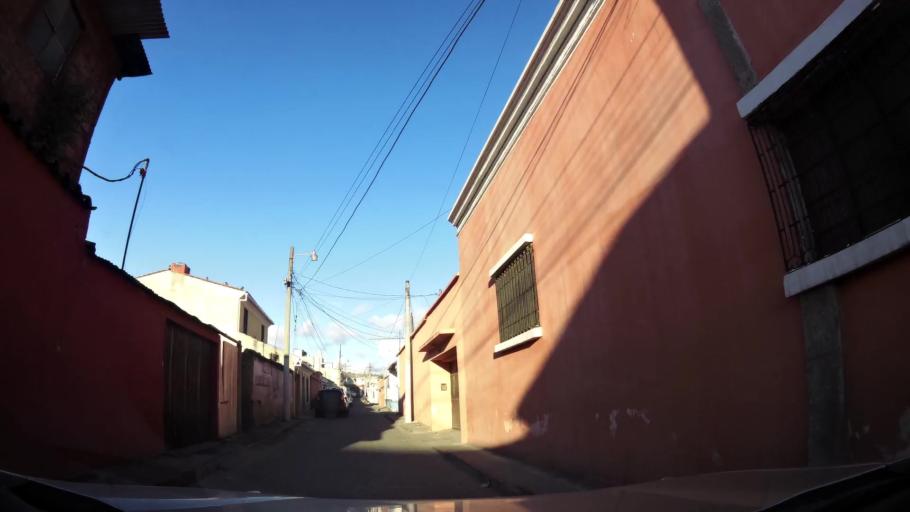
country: GT
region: Quetzaltenango
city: Quetzaltenango
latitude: 14.8377
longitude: -91.5249
